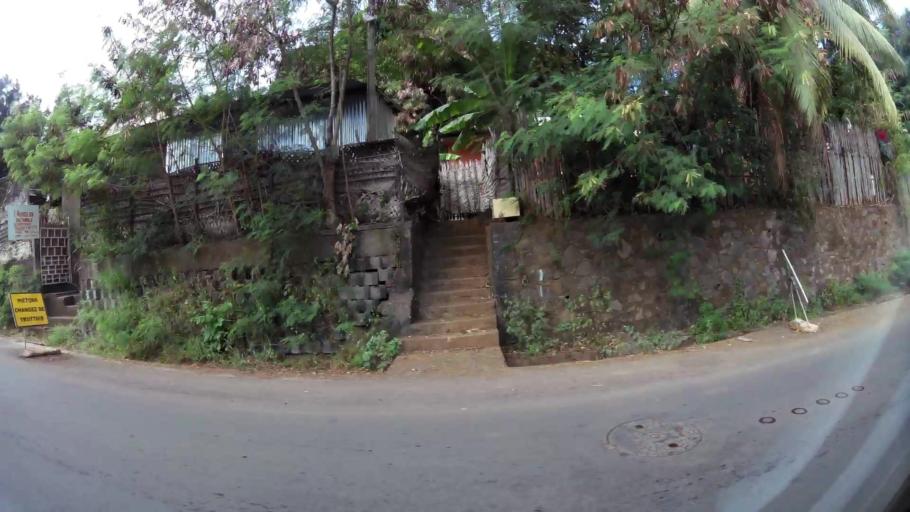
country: YT
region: Mamoudzou
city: Mamoudzou
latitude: -12.7820
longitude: 45.2237
